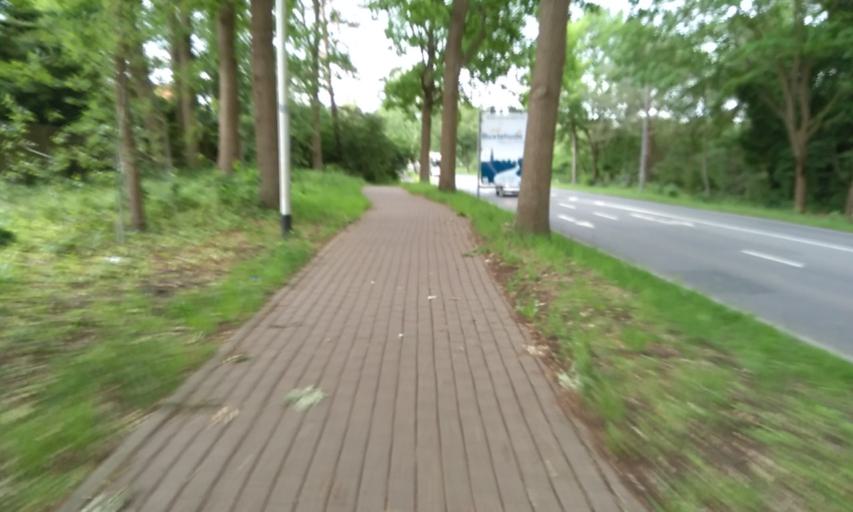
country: DE
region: Lower Saxony
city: Buxtehude
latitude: 53.4581
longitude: 9.6562
